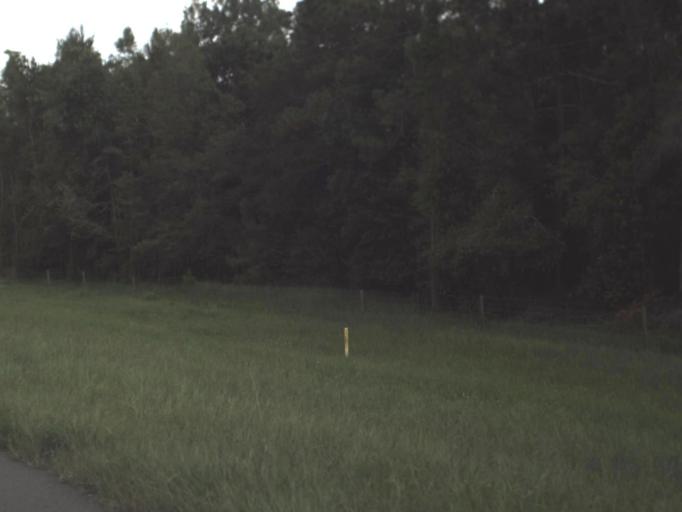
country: US
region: Florida
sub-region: Pasco County
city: Zephyrhills North
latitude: 28.2742
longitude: -82.1025
